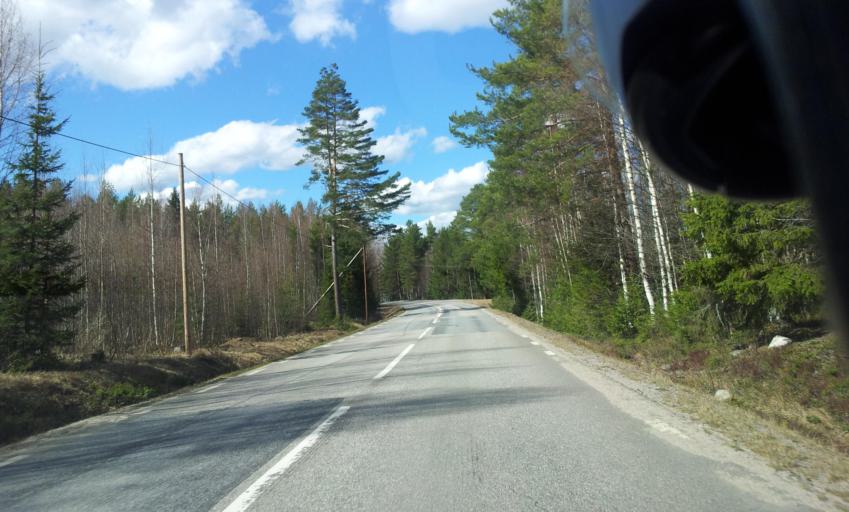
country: SE
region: Gaevleborg
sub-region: Ovanakers Kommun
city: Edsbyn
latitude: 61.3258
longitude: 15.8525
